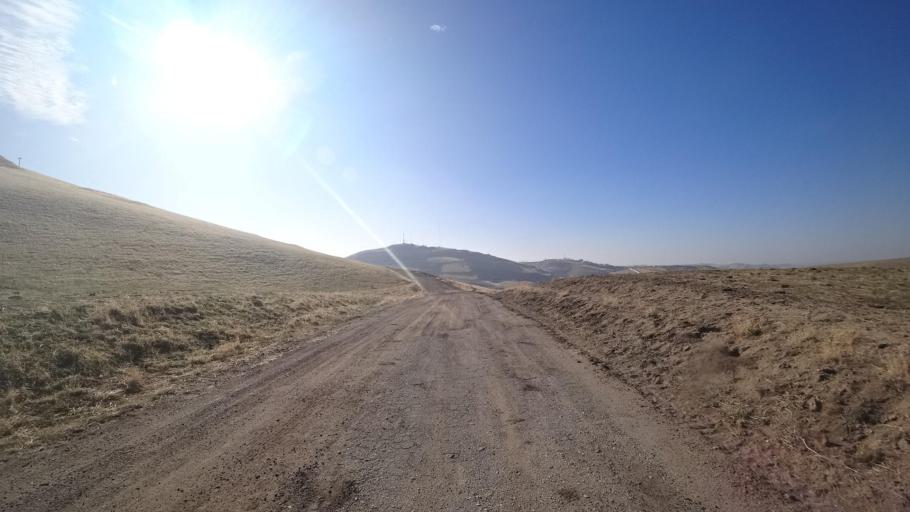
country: US
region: California
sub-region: Kern County
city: Oildale
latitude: 35.4914
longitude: -118.8789
